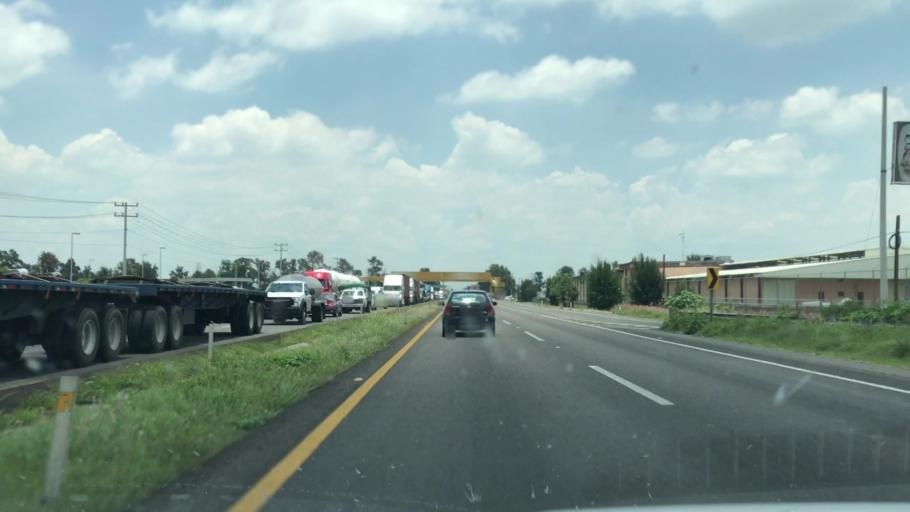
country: MX
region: Guanajuato
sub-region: Irapuato
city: Colonia Morelos de Guadalupe de Rivera
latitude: 20.5956
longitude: -101.4213
